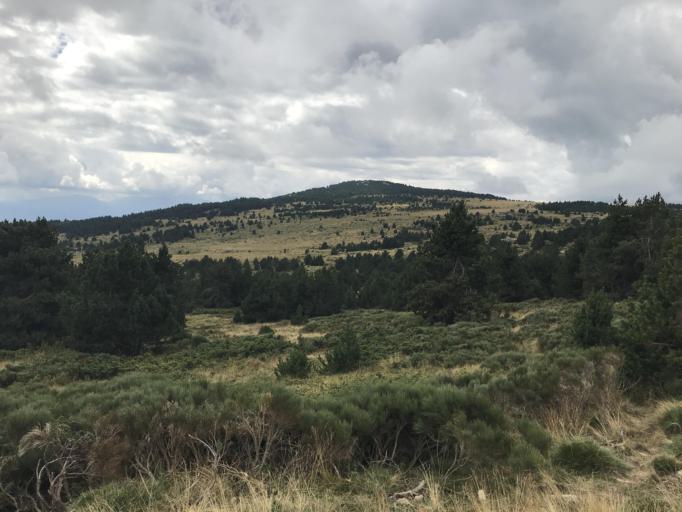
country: ES
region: Catalonia
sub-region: Provincia de Girona
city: Llivia
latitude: 42.5241
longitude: 2.0026
